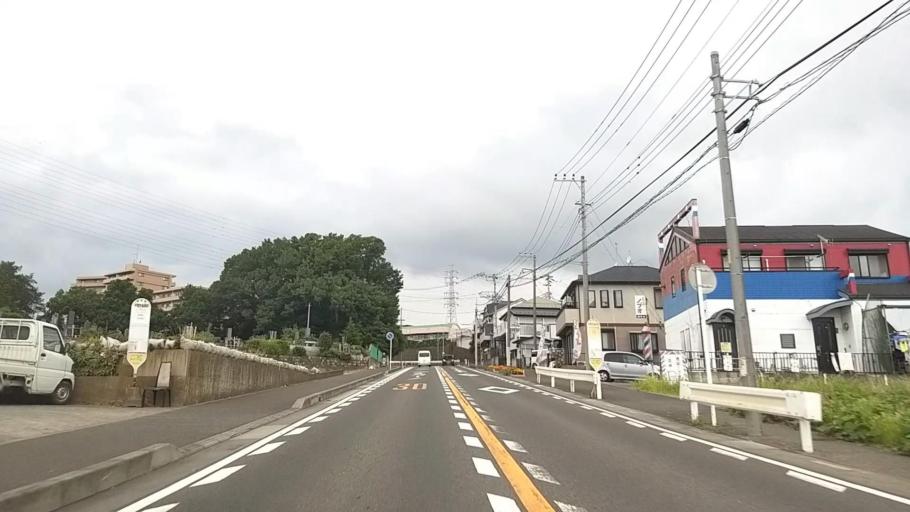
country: JP
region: Kanagawa
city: Isehara
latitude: 35.3903
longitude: 139.3246
